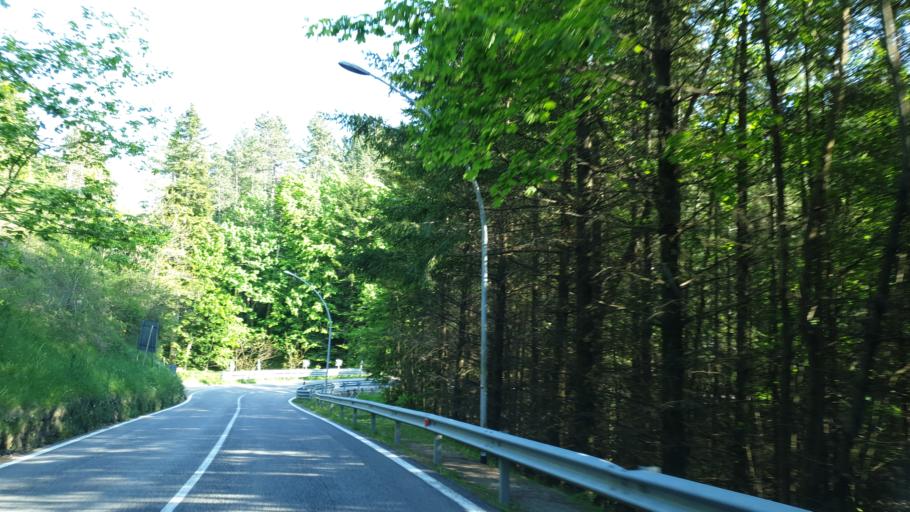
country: IT
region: Tuscany
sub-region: Province of Arezzo
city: Montemignaio
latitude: 43.7790
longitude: 11.5923
